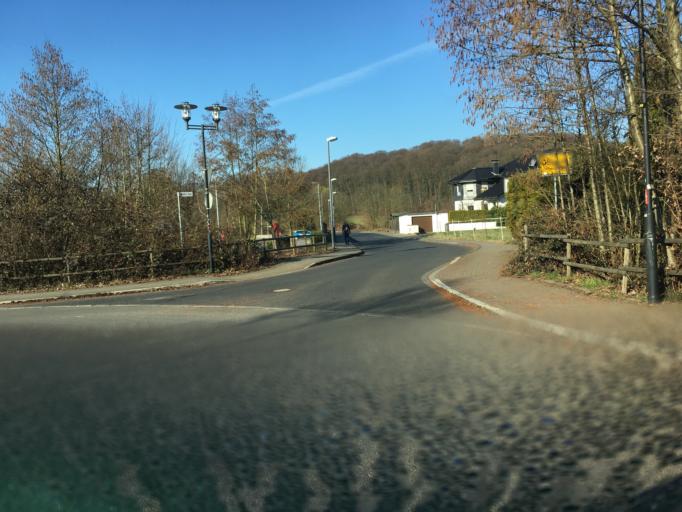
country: DE
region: North Rhine-Westphalia
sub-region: Regierungsbezirk Koln
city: Odenthal
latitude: 51.0299
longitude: 7.1037
